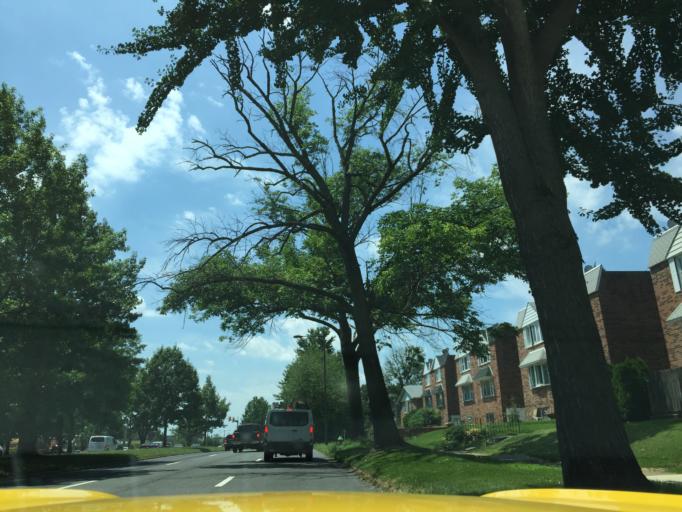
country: US
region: Pennsylvania
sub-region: Bucks County
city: Feasterville
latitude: 40.0860
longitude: -75.0242
